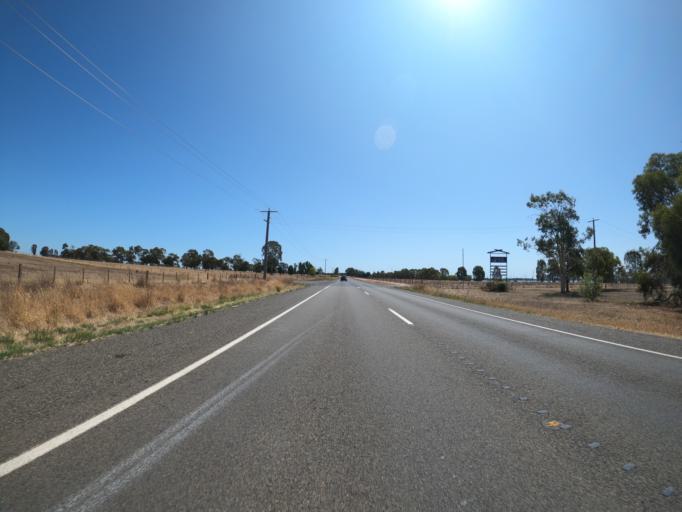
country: AU
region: Victoria
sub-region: Moira
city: Yarrawonga
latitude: -36.0267
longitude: 146.0854
